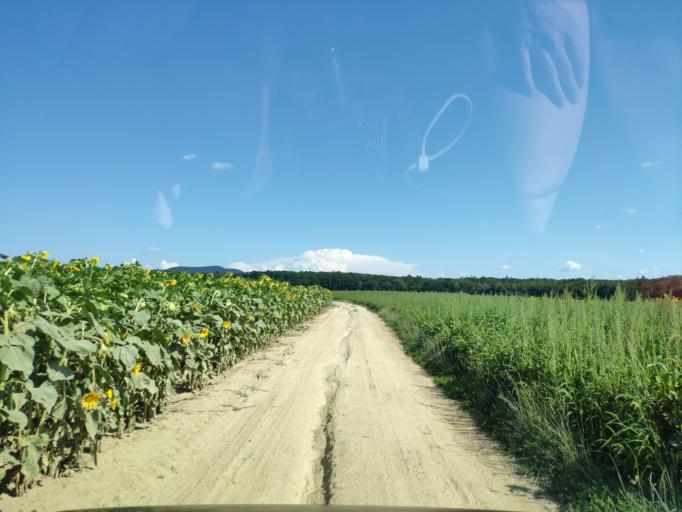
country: SK
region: Presovsky
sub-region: Okres Presov
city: Presov
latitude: 48.9063
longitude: 21.2757
